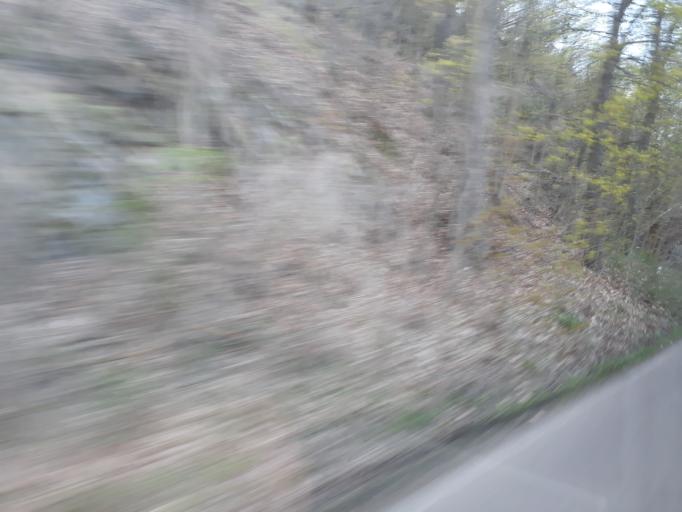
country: DE
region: Saxony
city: Kreischa
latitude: 50.9311
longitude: 13.7755
